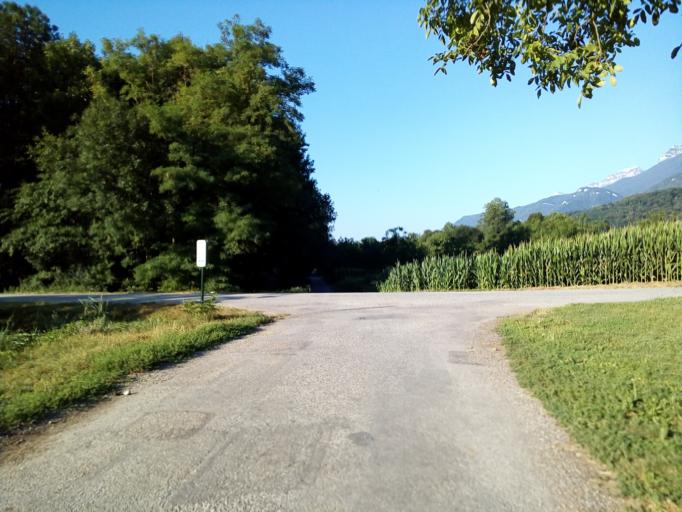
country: FR
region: Rhone-Alpes
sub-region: Departement de l'Isere
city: Le Cheylas
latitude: 45.4001
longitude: 5.9828
